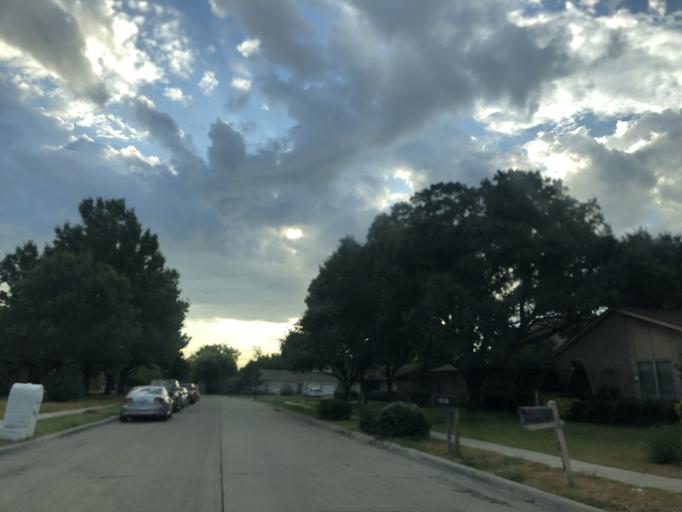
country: US
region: Texas
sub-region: Dallas County
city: Garland
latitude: 32.8752
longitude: -96.6551
